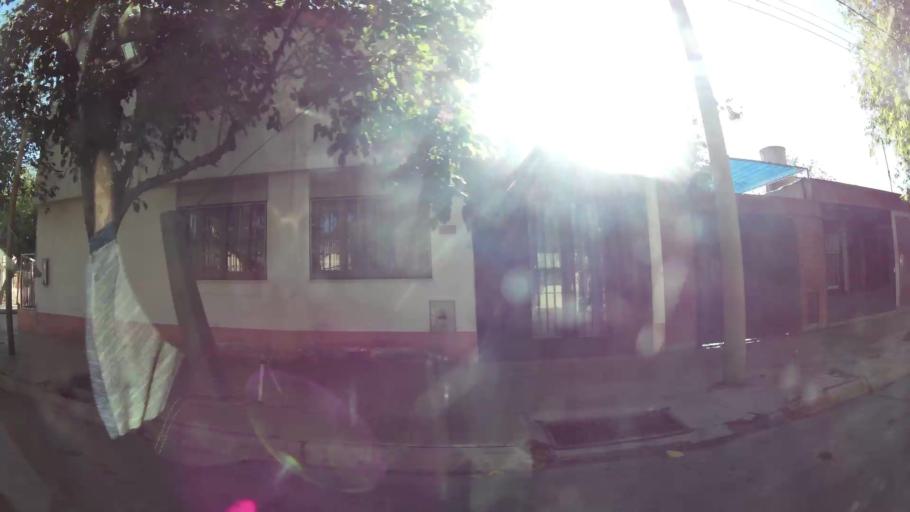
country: AR
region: San Juan
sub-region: Departamento de Santa Lucia
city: Santa Lucia
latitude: -31.5463
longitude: -68.5151
